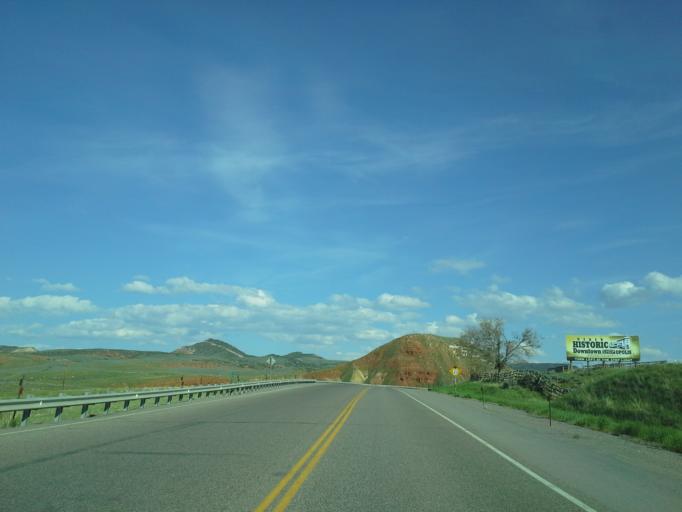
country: US
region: Wyoming
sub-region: Hot Springs County
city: Thermopolis
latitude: 43.6624
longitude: -108.2001
